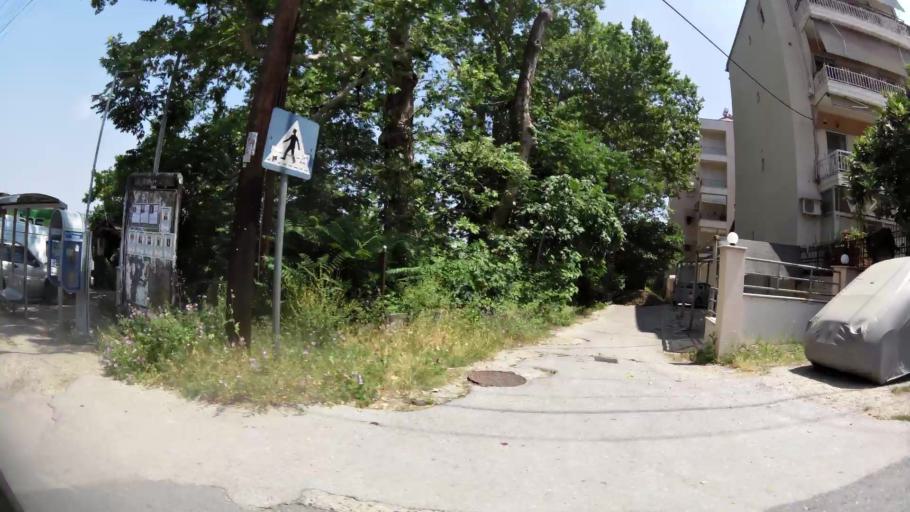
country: GR
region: Central Macedonia
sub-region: Nomos Imathias
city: Veroia
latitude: 40.5132
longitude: 22.2051
